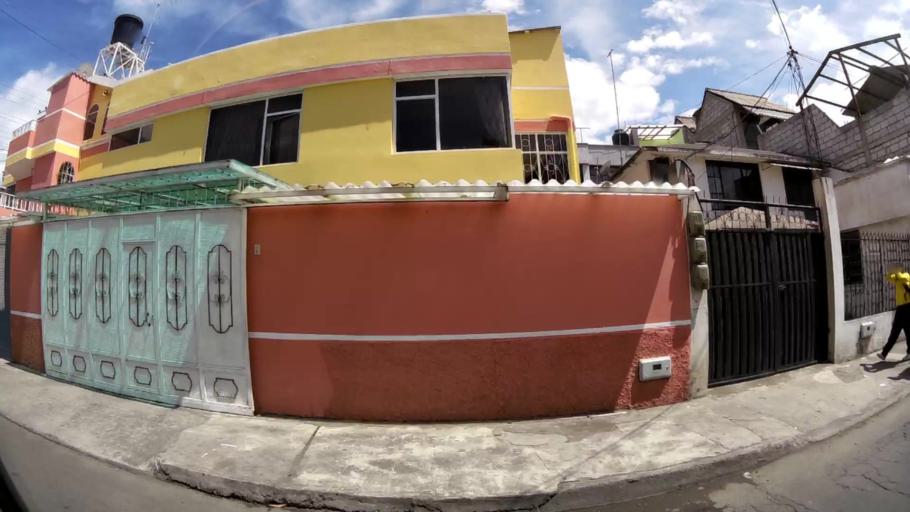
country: EC
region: Chimborazo
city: Riobamba
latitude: -1.6580
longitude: -78.6435
